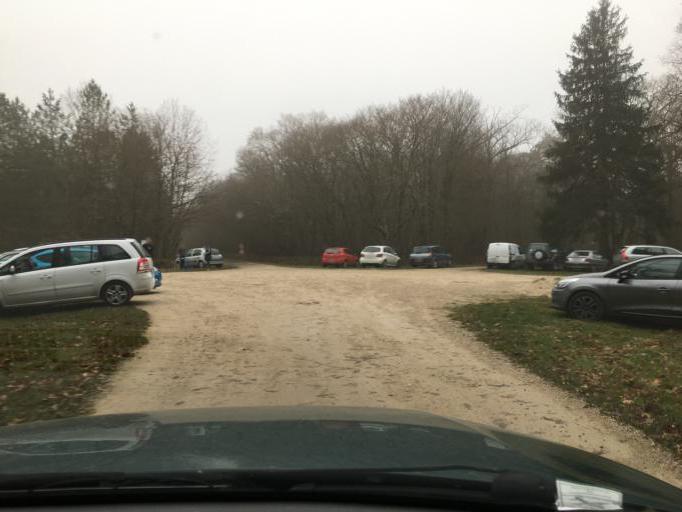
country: FR
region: Centre
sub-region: Departement du Loiret
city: Saran
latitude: 47.9834
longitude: 1.8984
